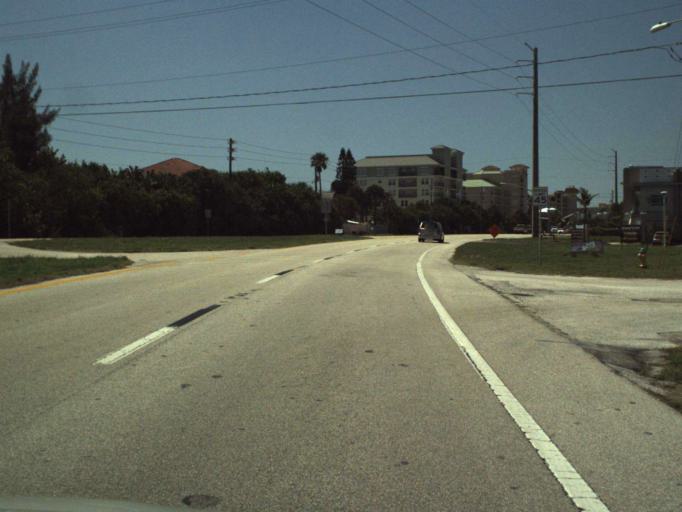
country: US
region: Florida
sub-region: Brevard County
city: Cocoa Beach
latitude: 28.2847
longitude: -80.6080
